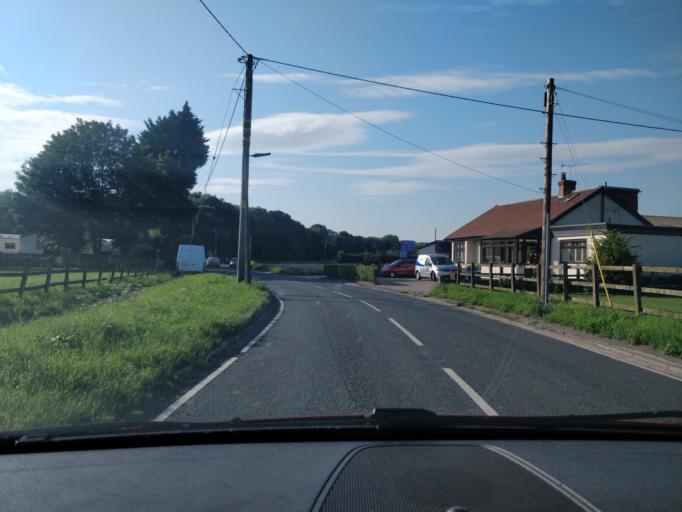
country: GB
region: England
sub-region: Lancashire
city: Banks
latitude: 53.6515
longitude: -2.8758
